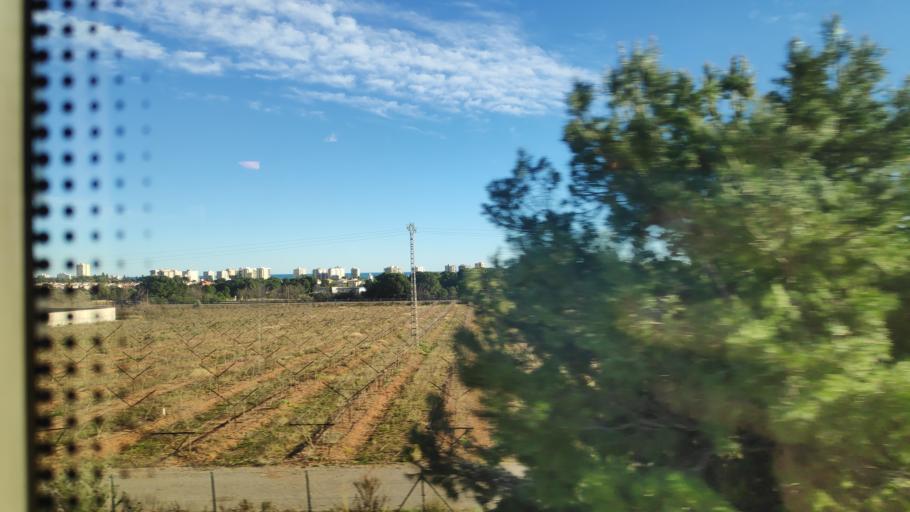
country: ES
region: Valencia
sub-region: Provincia de Castello
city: Benicassim
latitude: 40.0428
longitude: 0.0362
